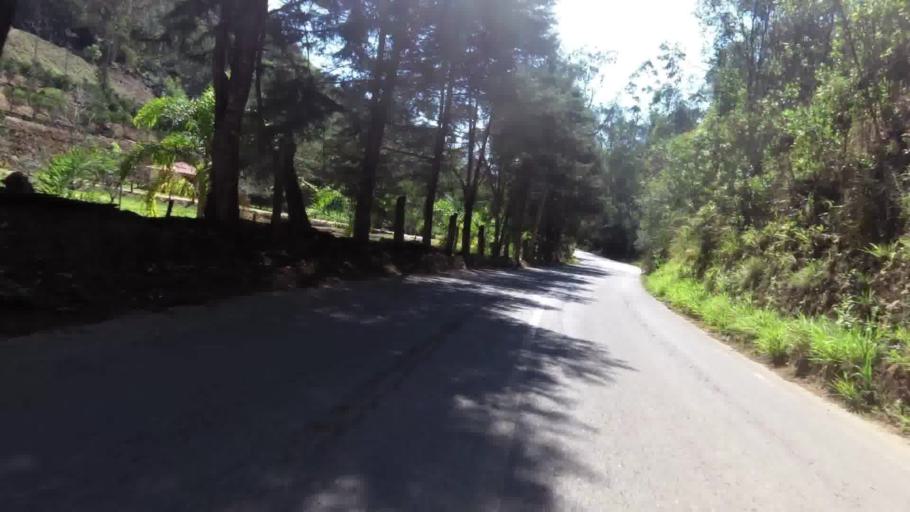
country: BR
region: Espirito Santo
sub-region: Marechal Floriano
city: Marechal Floriano
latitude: -20.4438
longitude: -40.8846
